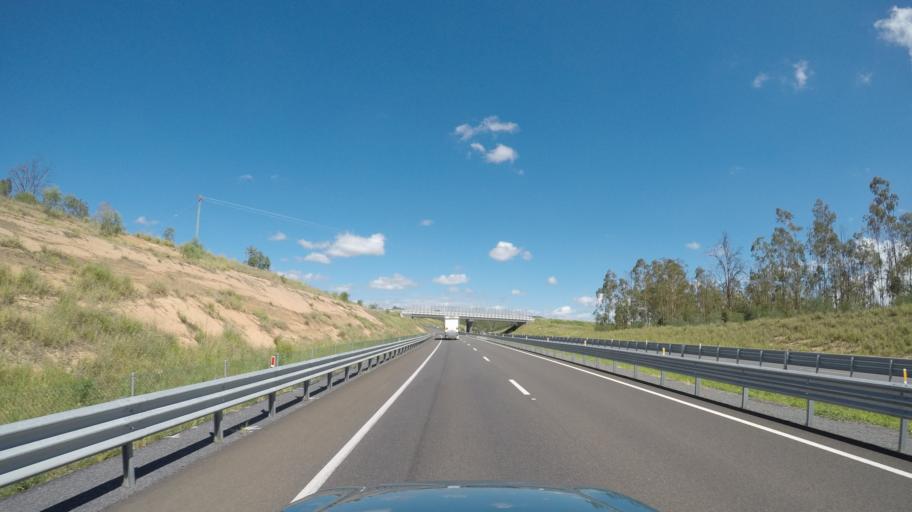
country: AU
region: Queensland
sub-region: Toowoomba
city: East Toowoomba
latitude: -27.5248
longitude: 152.0666
